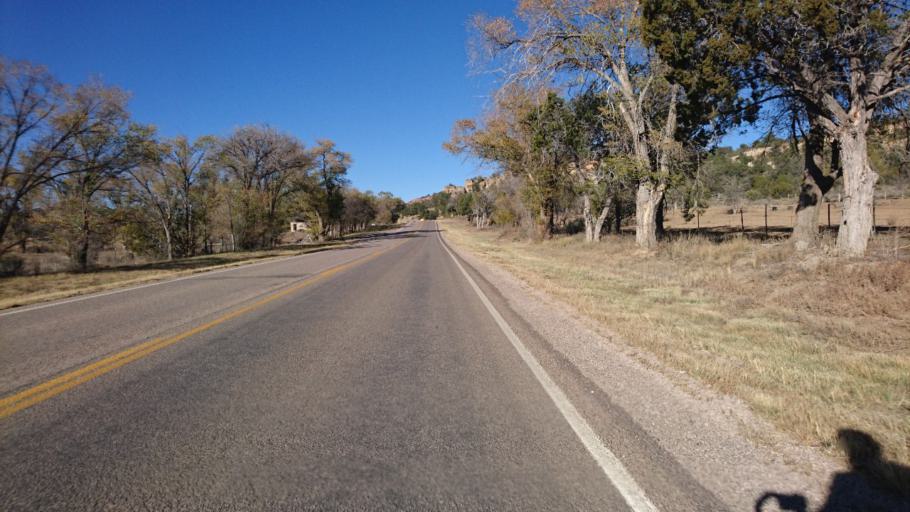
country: US
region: New Mexico
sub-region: McKinley County
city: Black Rock
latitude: 35.1333
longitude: -108.5127
